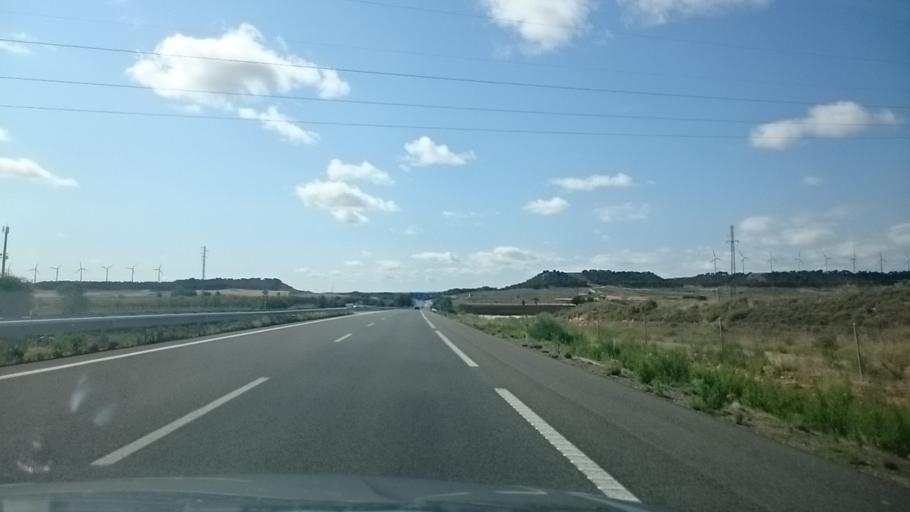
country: ES
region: Navarre
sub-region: Provincia de Navarra
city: Corella
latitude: 42.1029
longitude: -1.7266
